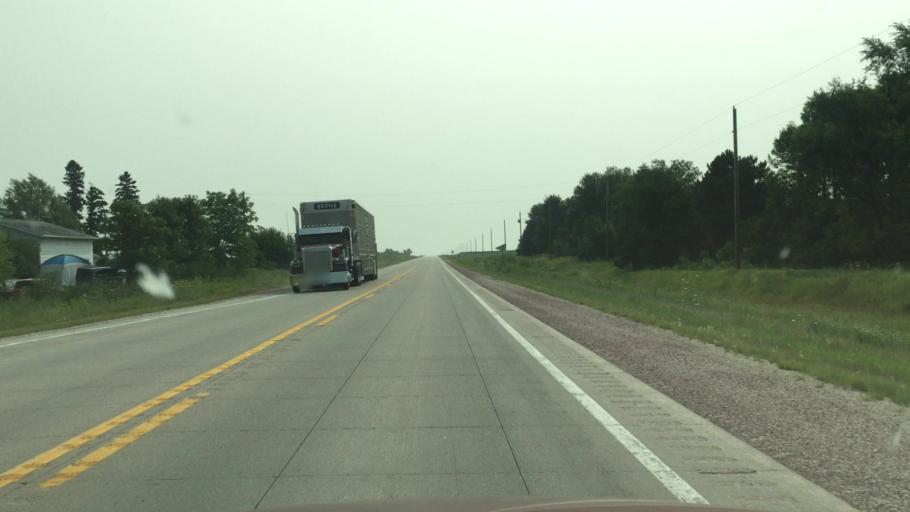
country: US
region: Iowa
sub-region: Osceola County
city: Sibley
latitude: 43.4328
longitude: -95.6423
